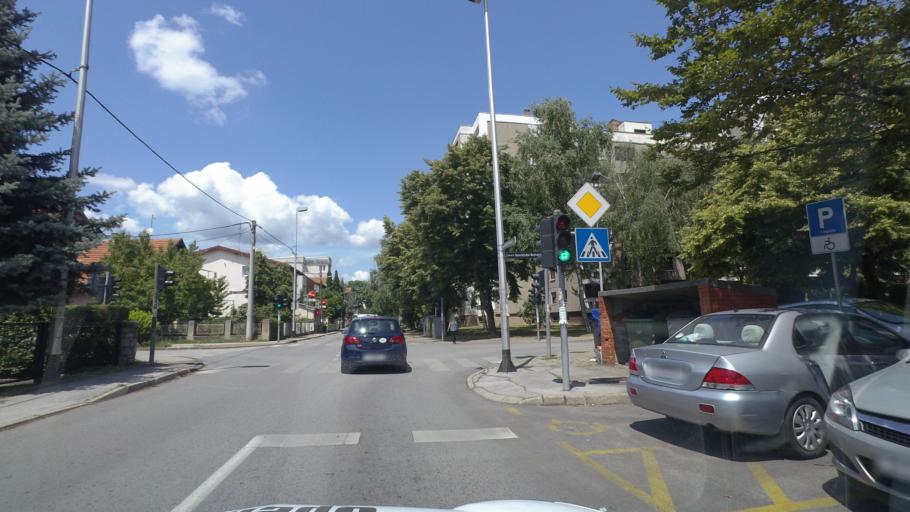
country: HR
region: Grad Zagreb
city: Dubrava
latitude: 45.8158
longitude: 16.0261
